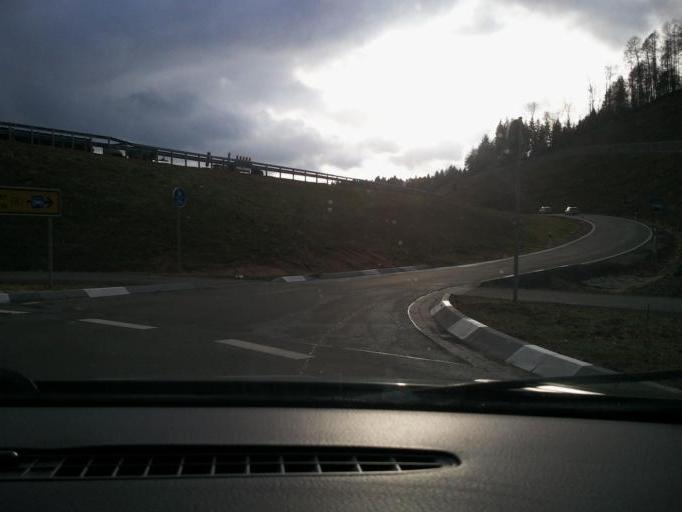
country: DE
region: Rheinland-Pfalz
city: Hinterweidenthal
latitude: 49.2012
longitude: 7.7427
